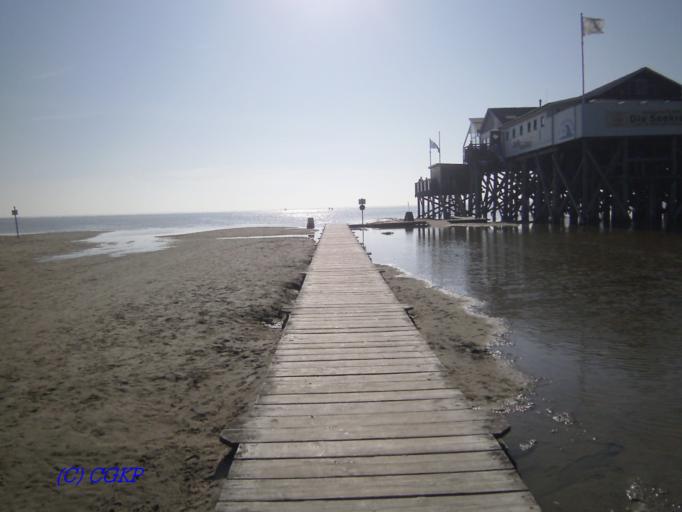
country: DE
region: Schleswig-Holstein
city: Sankt Peter-Ording
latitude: 54.2731
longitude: 8.6566
